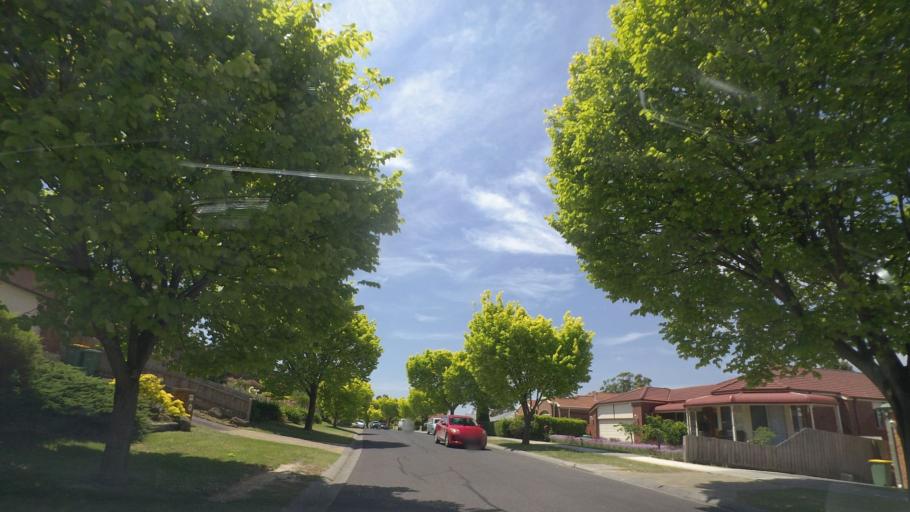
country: AU
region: Victoria
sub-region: Yarra Ranges
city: Chirnside Park
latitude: -37.7516
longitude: 145.3065
